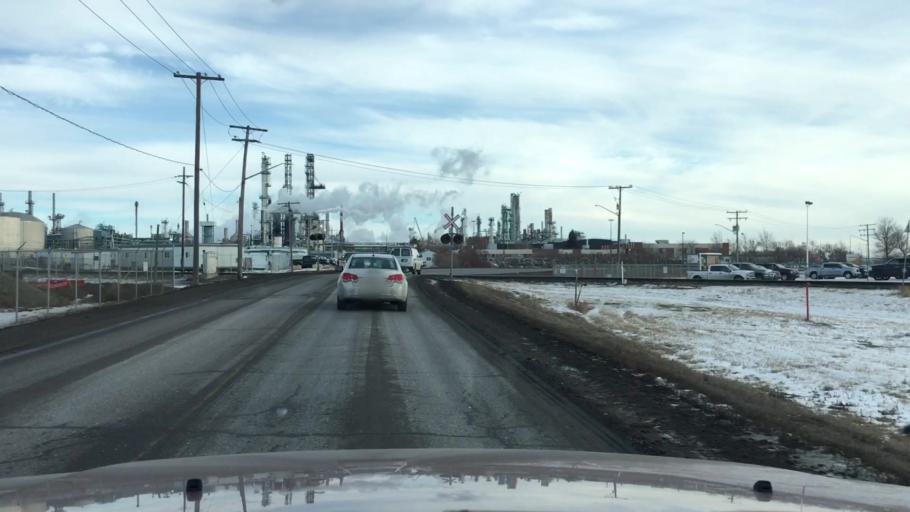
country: CA
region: Saskatchewan
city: Regina
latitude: 50.4843
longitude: -104.5834
